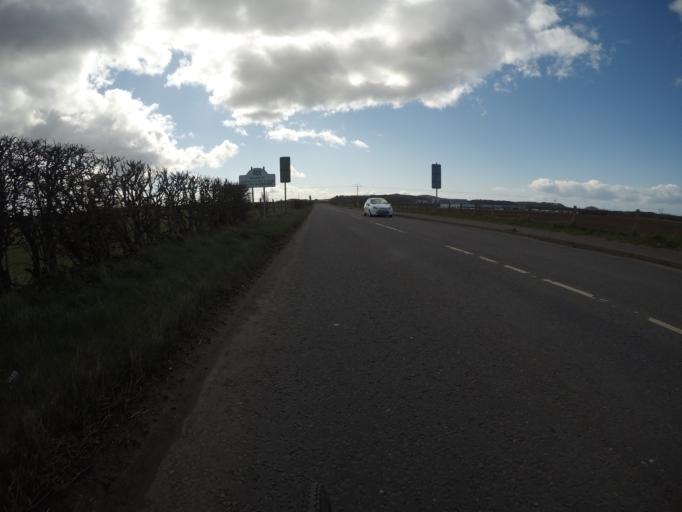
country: GB
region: Scotland
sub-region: North Ayrshire
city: Dreghorn
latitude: 55.5934
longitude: -4.6030
